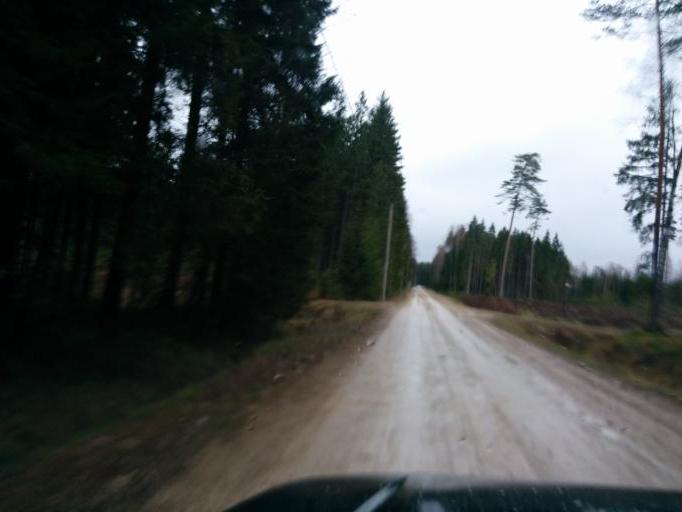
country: LV
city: Tireli
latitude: 56.8191
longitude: 23.6939
